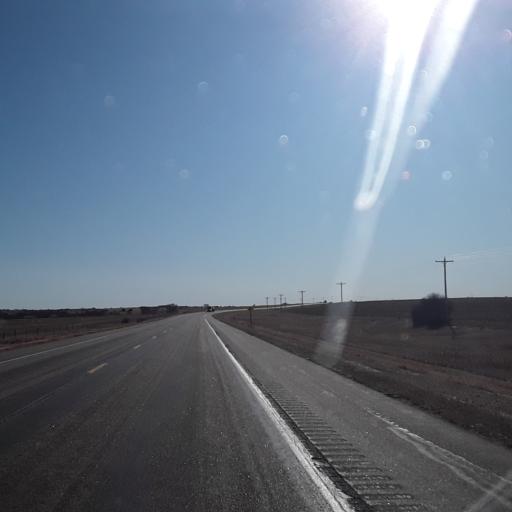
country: US
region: Nebraska
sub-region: Frontier County
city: Stockville
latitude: 40.5688
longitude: -100.6299
